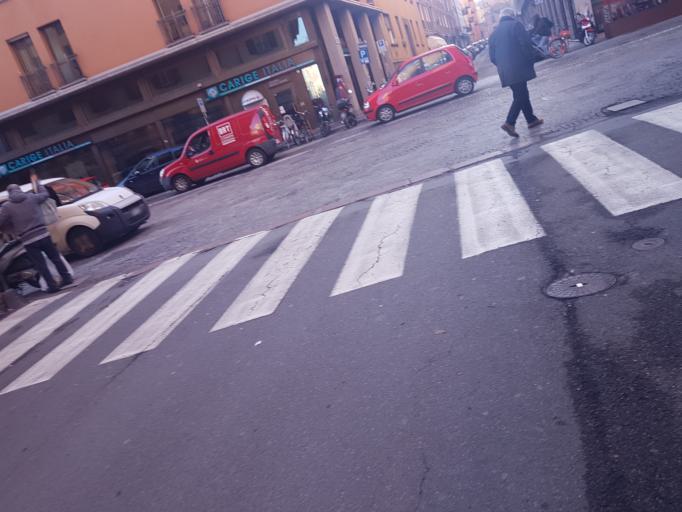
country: IT
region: Emilia-Romagna
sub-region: Provincia di Bologna
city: Bologna
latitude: 44.4990
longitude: 11.3395
